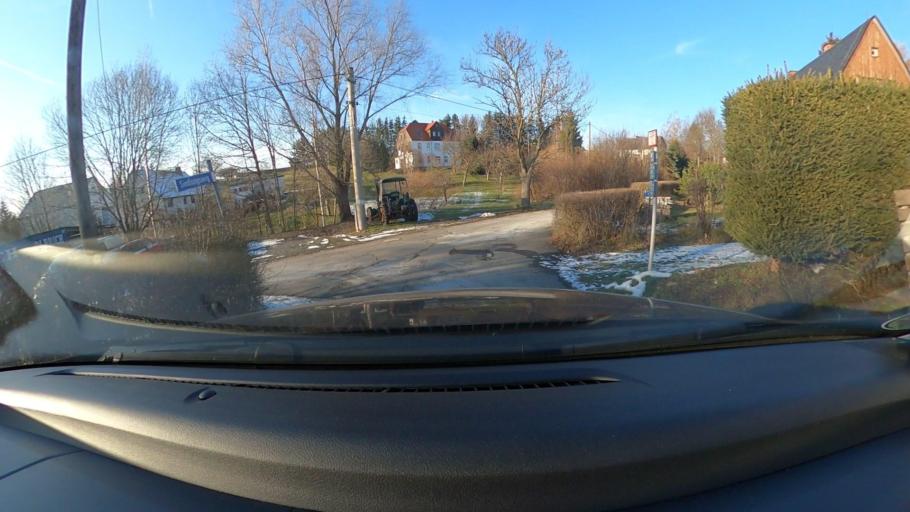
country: DE
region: Saxony
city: Frankenstein
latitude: 50.9409
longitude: 13.2172
